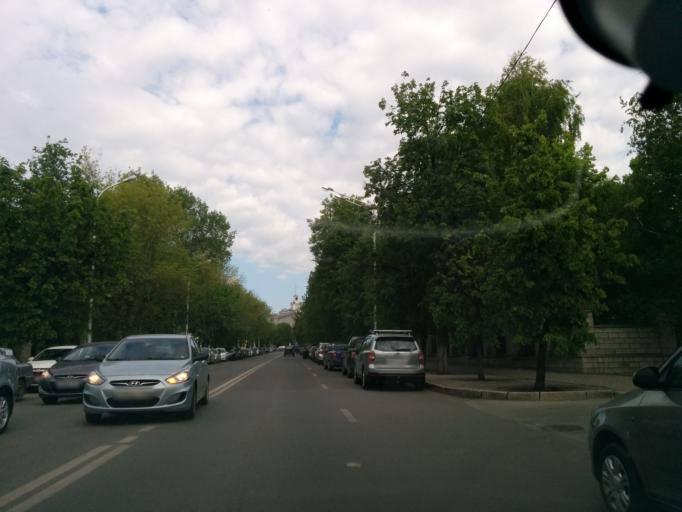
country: RU
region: Bashkortostan
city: Ufa
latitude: 54.7196
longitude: 55.9538
